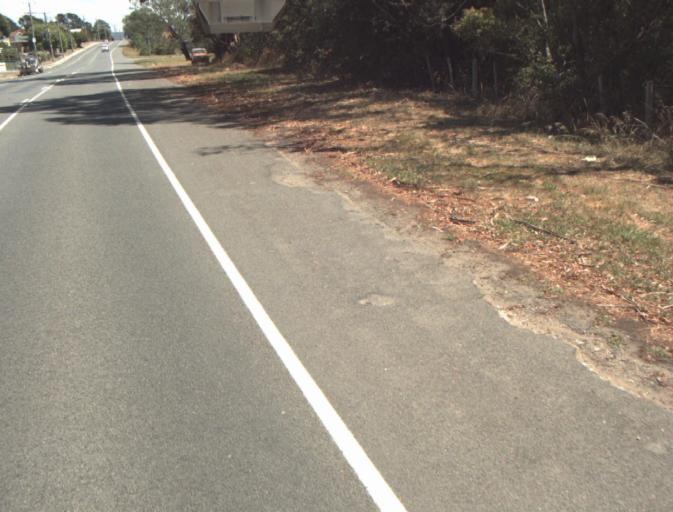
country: AU
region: Tasmania
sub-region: Launceston
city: Mayfield
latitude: -41.3721
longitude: 147.1378
